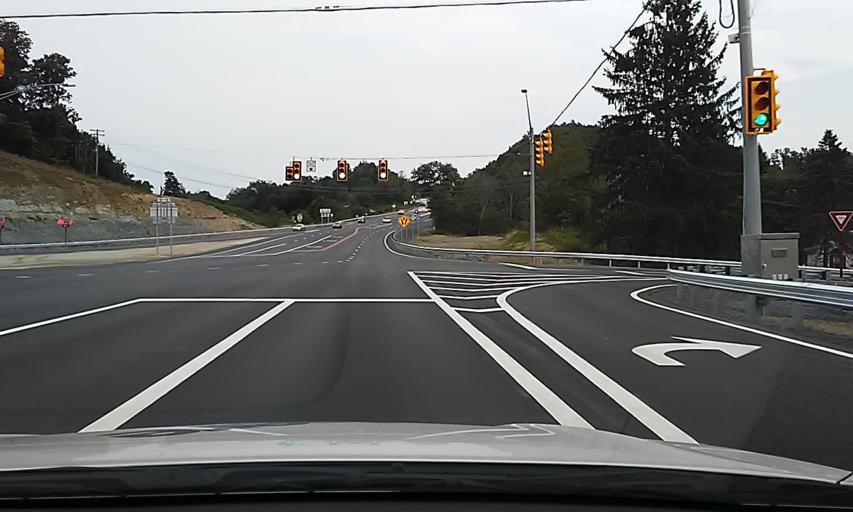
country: US
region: West Virginia
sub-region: Monongalia County
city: Brookhaven
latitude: 39.6525
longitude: -79.9138
